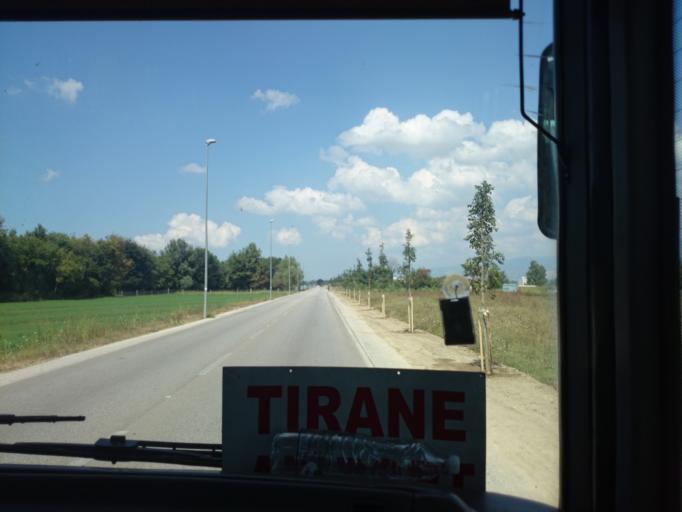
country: AL
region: Tirane
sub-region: Rrethi i Tiranes
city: Berxull
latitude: 41.3954
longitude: 19.7042
